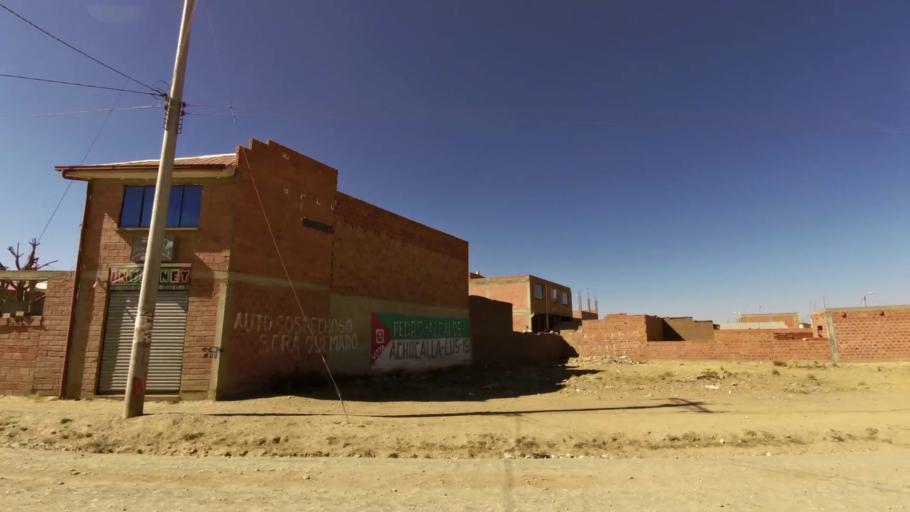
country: BO
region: La Paz
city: La Paz
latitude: -16.6239
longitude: -68.1905
